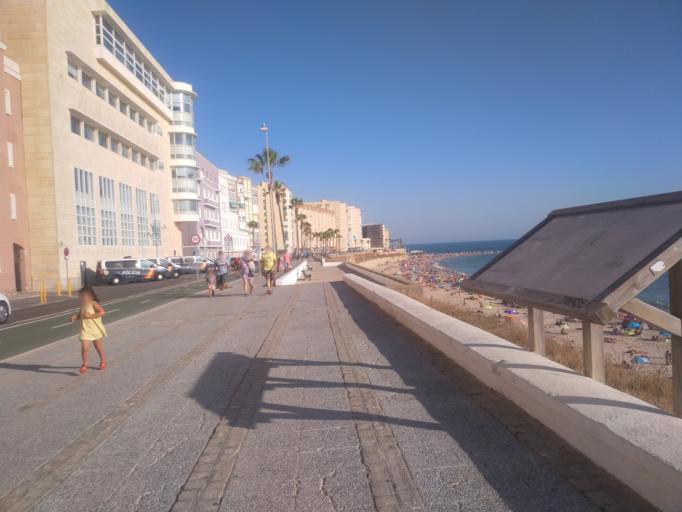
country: ES
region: Andalusia
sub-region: Provincia de Cadiz
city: Cadiz
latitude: 36.5228
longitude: -6.2875
